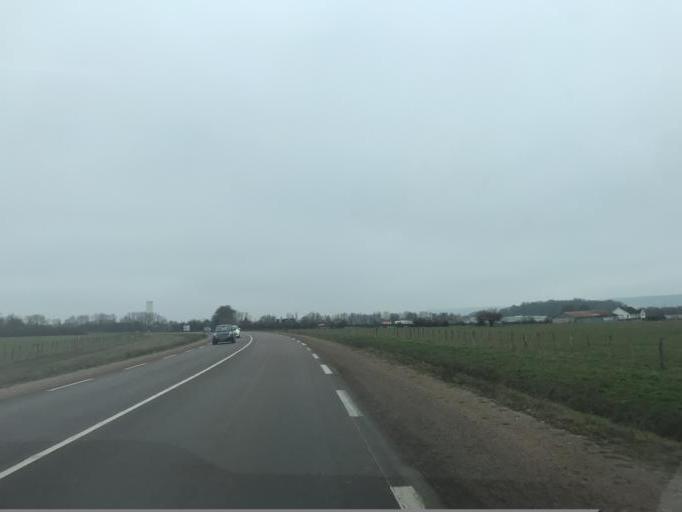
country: FR
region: Bourgogne
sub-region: Departement de l'Yonne
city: Avallon
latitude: 47.5017
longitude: 3.9046
